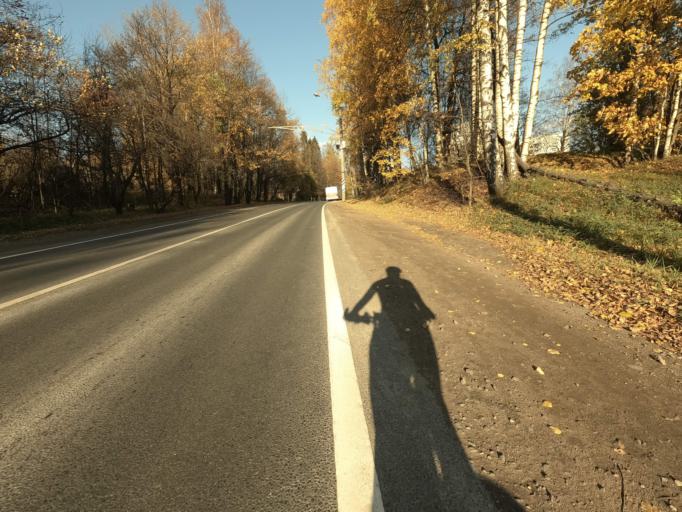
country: RU
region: St.-Petersburg
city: Pargolovo
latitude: 60.1078
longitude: 30.2490
